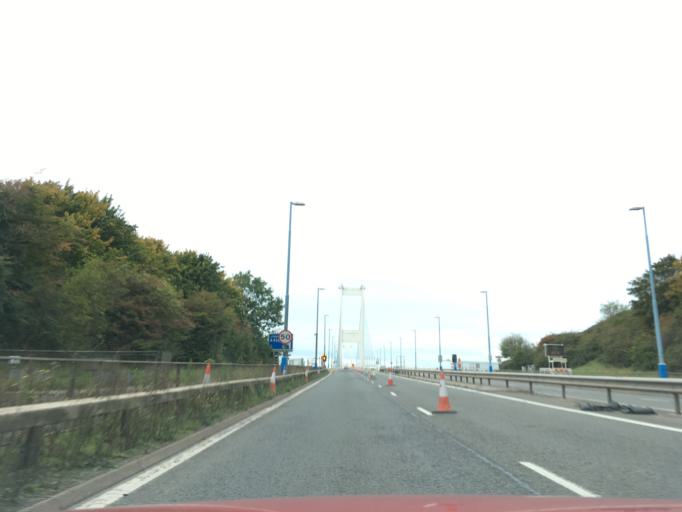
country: GB
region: England
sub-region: South Gloucestershire
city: Severn Beach
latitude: 51.6045
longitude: -2.6261
